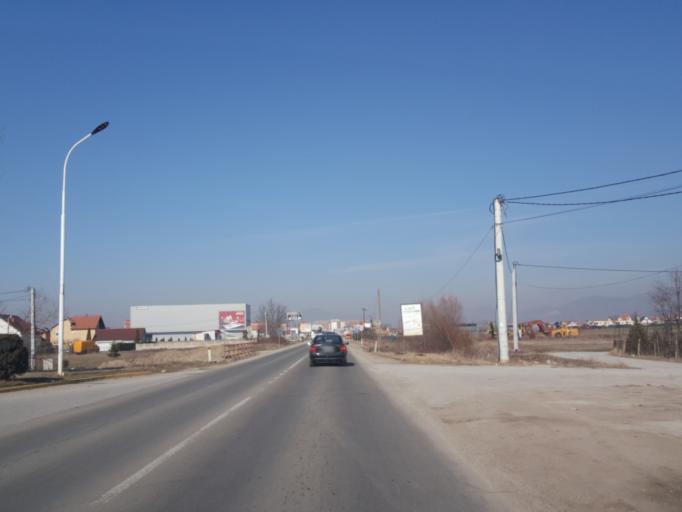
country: XK
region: Mitrovica
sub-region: Vushtrri
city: Vushtrri
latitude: 42.8093
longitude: 20.9878
